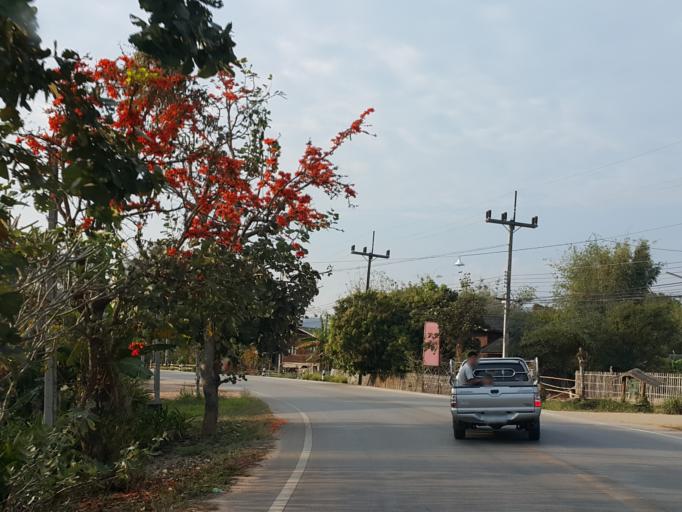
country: TH
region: Lampang
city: Chae Hom
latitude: 18.5433
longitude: 99.4804
